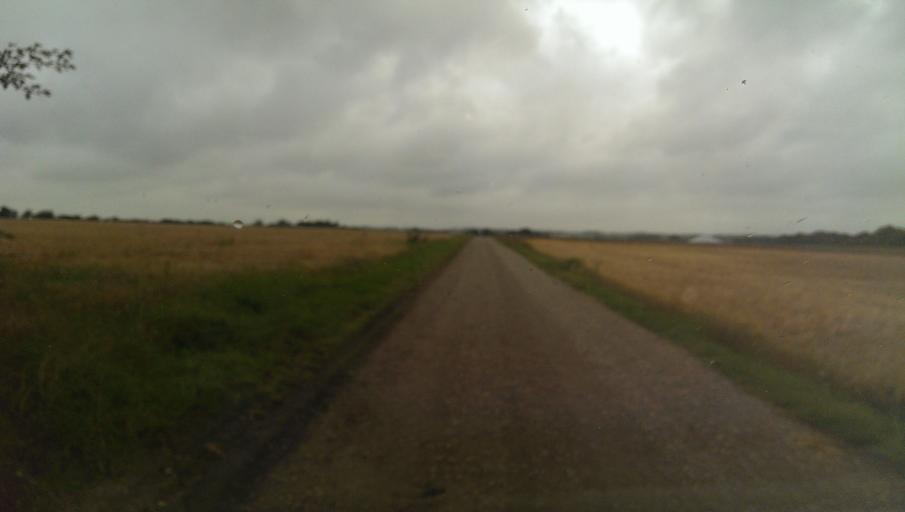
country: DK
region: South Denmark
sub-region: Esbjerg Kommune
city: Tjaereborg
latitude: 55.4846
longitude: 8.5993
